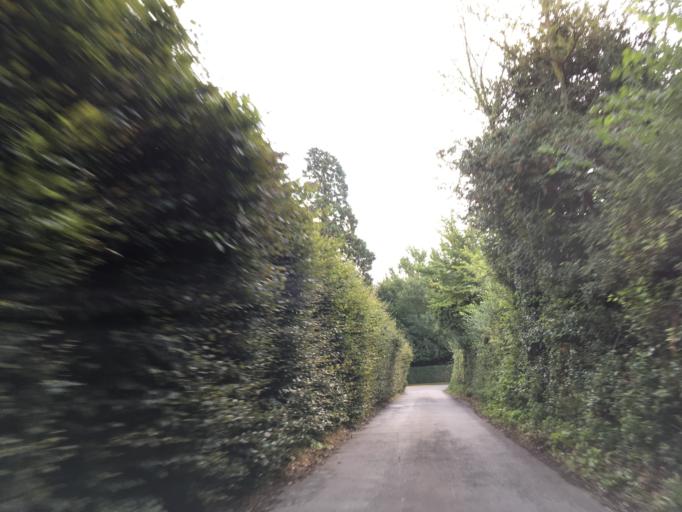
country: GB
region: England
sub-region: Hampshire
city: Andover
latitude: 51.1967
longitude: -1.3820
